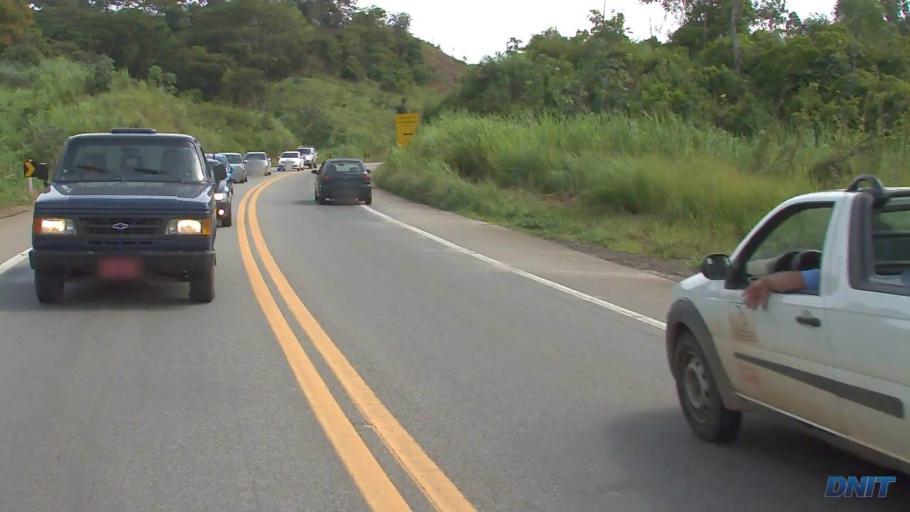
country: BR
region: Minas Gerais
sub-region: Ipaba
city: Ipaba
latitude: -19.3826
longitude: -42.4680
